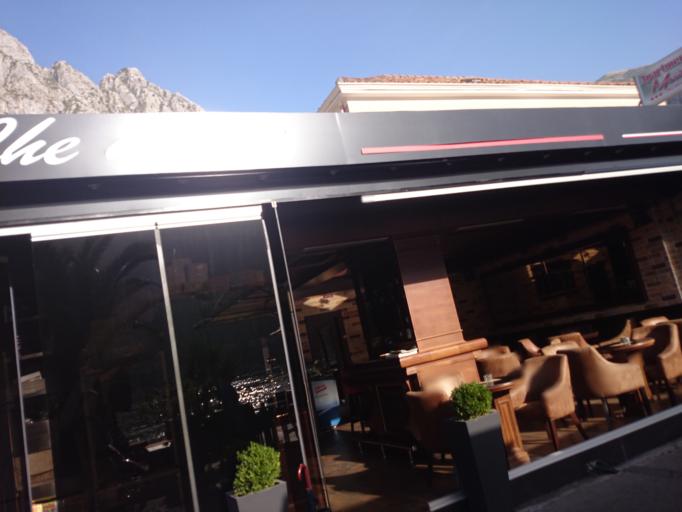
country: ME
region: Kotor
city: Kotor
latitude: 42.4319
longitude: 18.7673
